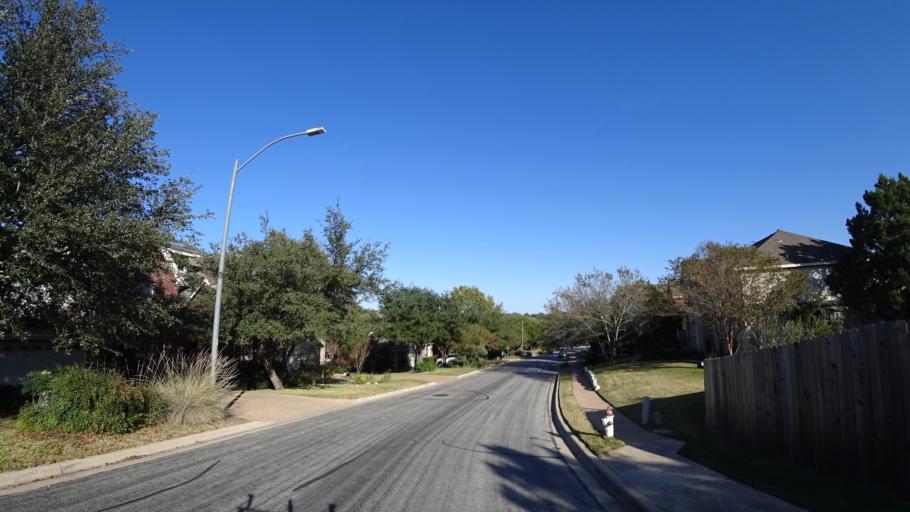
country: US
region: Texas
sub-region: Williamson County
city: Jollyville
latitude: 30.4121
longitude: -97.7775
